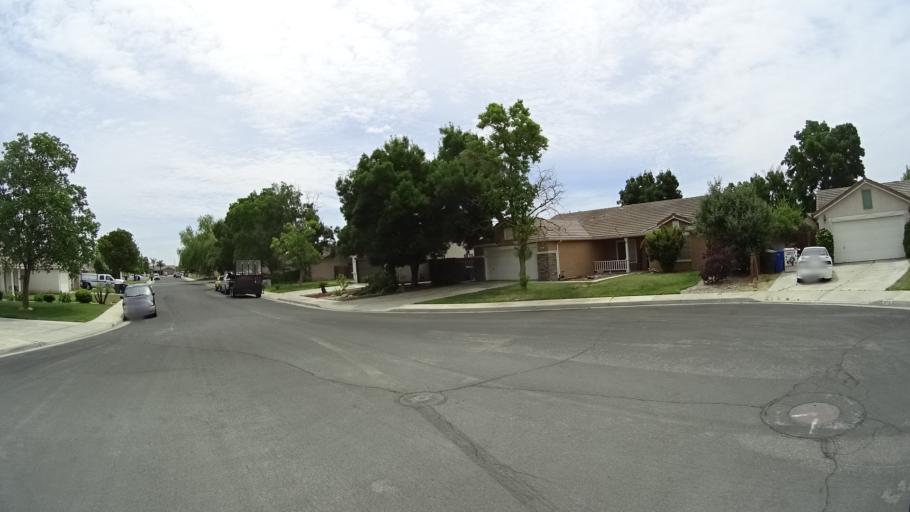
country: US
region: California
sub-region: Kings County
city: Lucerne
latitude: 36.3677
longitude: -119.6400
